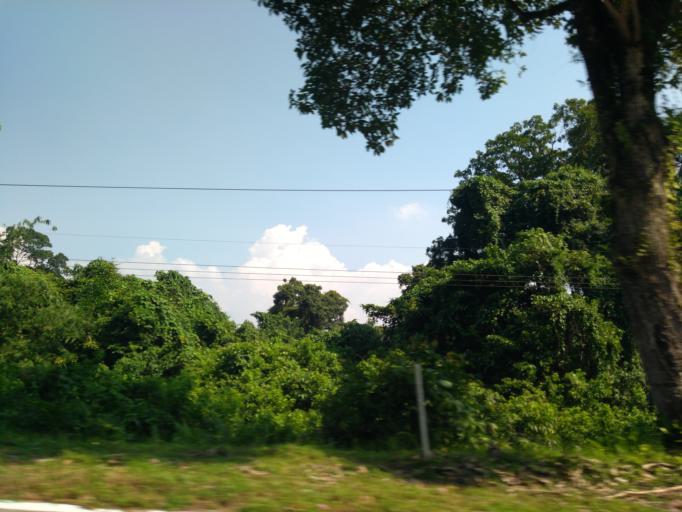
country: MY
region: Sarawak
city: Kuching
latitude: 1.7277
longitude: 110.3170
